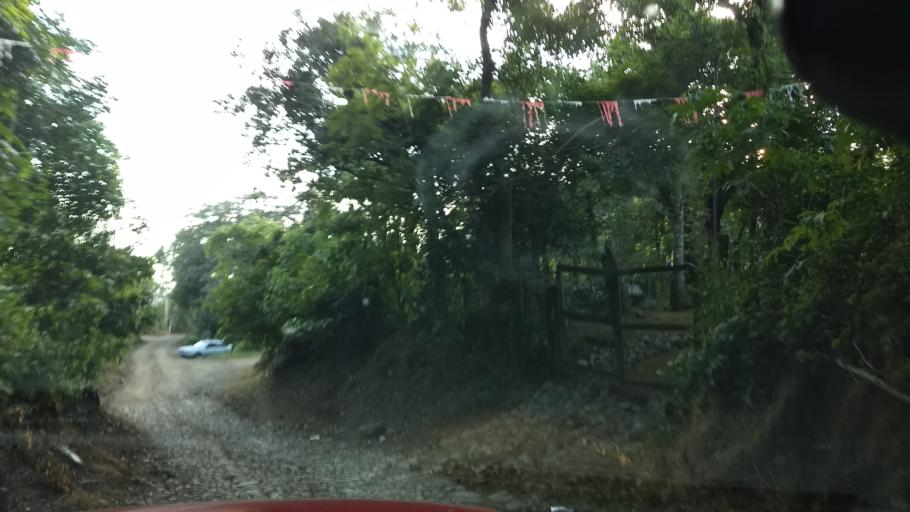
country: MX
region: Jalisco
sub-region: San Gabriel
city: Alista
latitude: 19.5089
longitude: -103.7523
